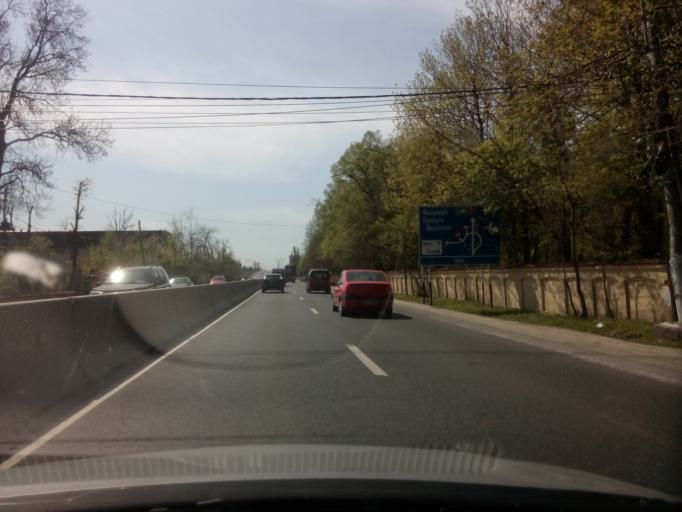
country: RO
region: Ilfov
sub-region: Comuna Otopeni
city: Otopeni
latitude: 44.5780
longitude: 26.0701
